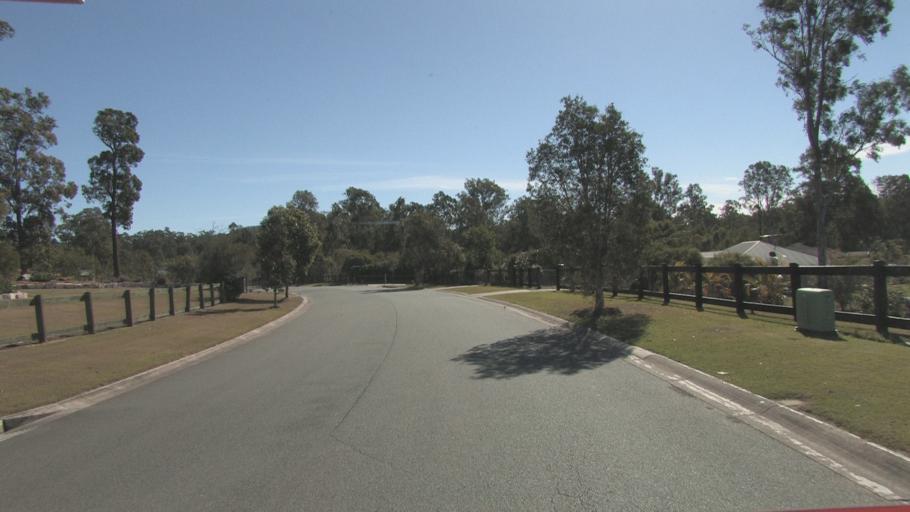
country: AU
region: Queensland
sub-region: Ipswich
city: Springfield Lakes
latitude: -27.7416
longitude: 152.9219
